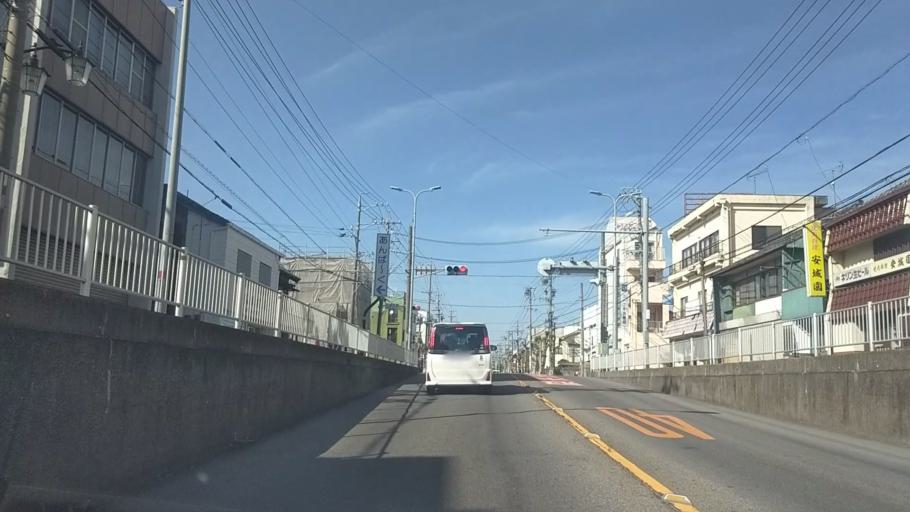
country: JP
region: Aichi
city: Anjo
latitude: 34.9622
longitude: 137.0840
